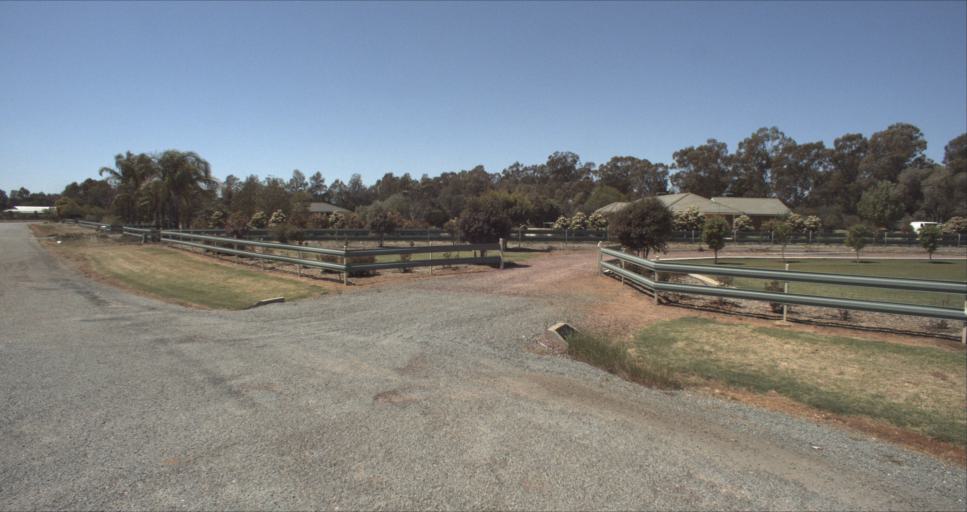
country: AU
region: New South Wales
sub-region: Leeton
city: Leeton
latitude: -34.5318
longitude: 146.3949
